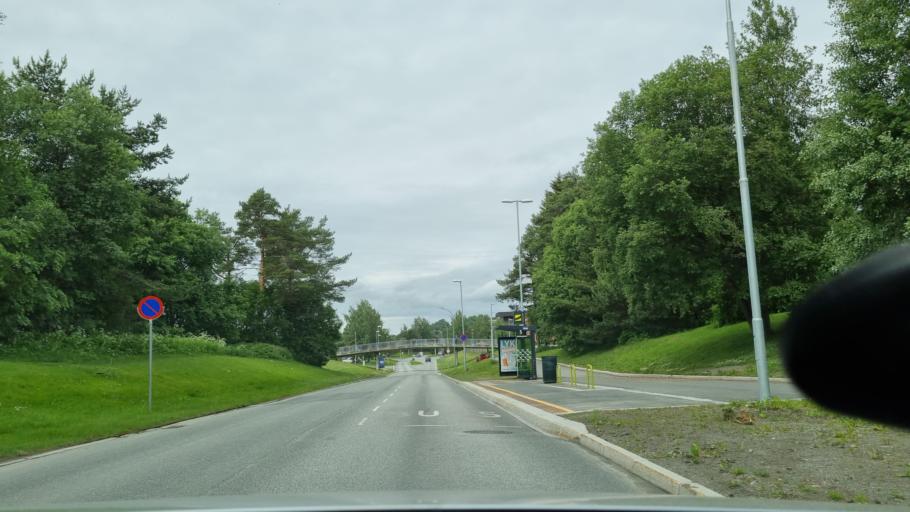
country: NO
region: Sor-Trondelag
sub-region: Melhus
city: Melhus
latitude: 63.3456
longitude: 10.3387
